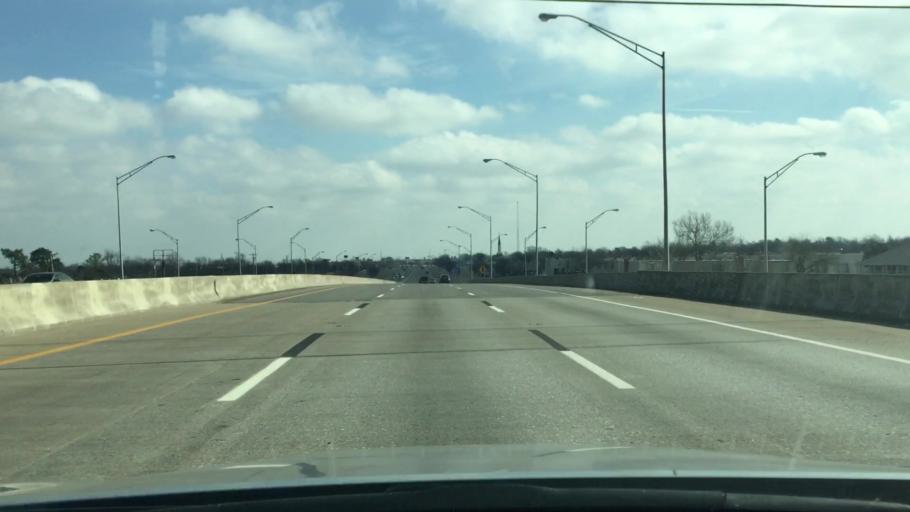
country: US
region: Oklahoma
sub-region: Oklahoma County
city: Oklahoma City
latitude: 35.3939
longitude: -97.5654
